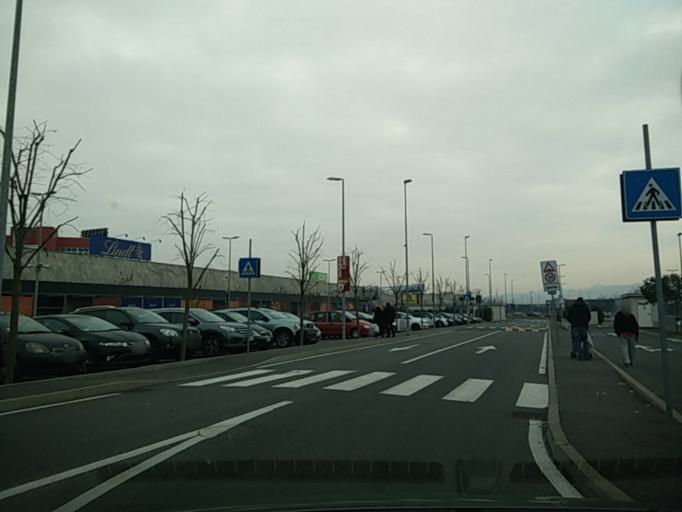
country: IT
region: Piedmont
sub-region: Provincia di Torino
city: Settimo Torinese
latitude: 45.1385
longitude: 7.7320
